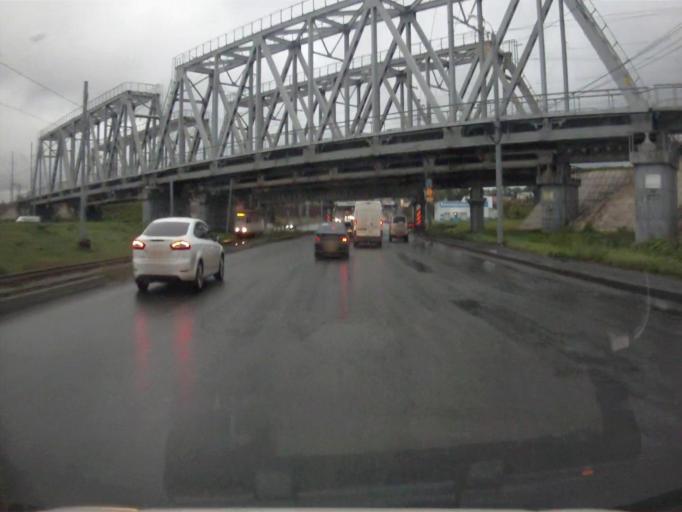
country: RU
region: Chelyabinsk
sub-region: Gorod Chelyabinsk
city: Chelyabinsk
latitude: 55.1547
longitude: 61.4431
